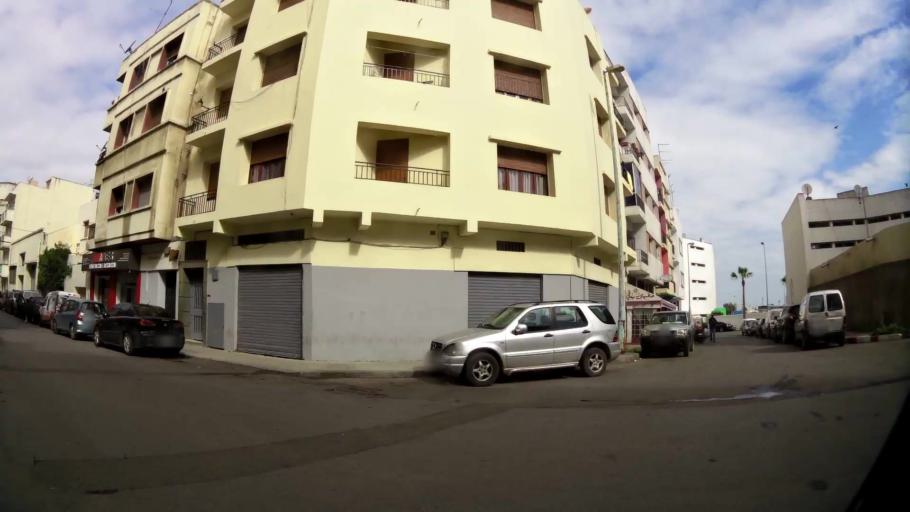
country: MA
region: Grand Casablanca
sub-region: Casablanca
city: Casablanca
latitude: 33.5963
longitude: -7.5905
